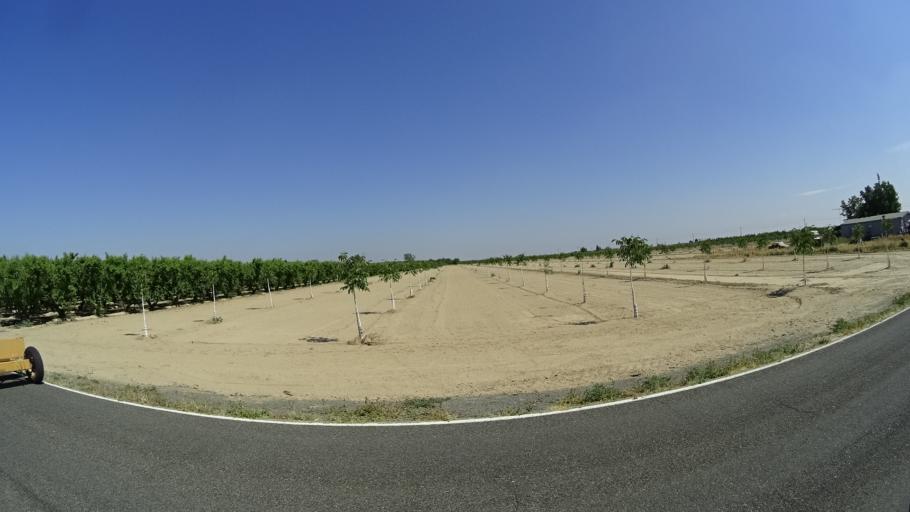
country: US
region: California
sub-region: Fresno County
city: Kingsburg
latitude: 36.4524
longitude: -119.5861
